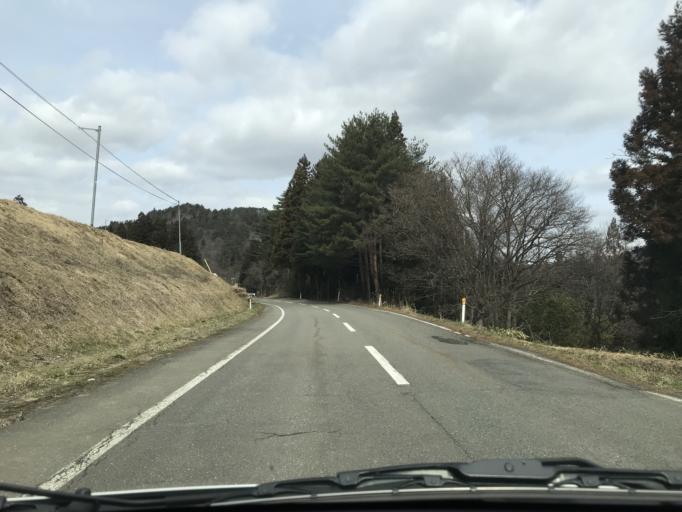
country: JP
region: Iwate
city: Kitakami
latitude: 39.2787
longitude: 141.3201
